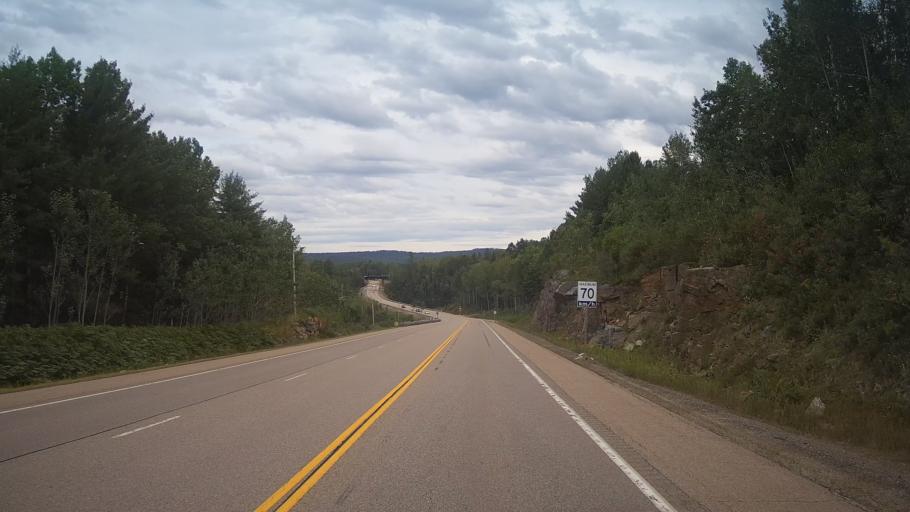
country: CA
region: Ontario
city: Deep River
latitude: 46.2303
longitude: -78.0748
